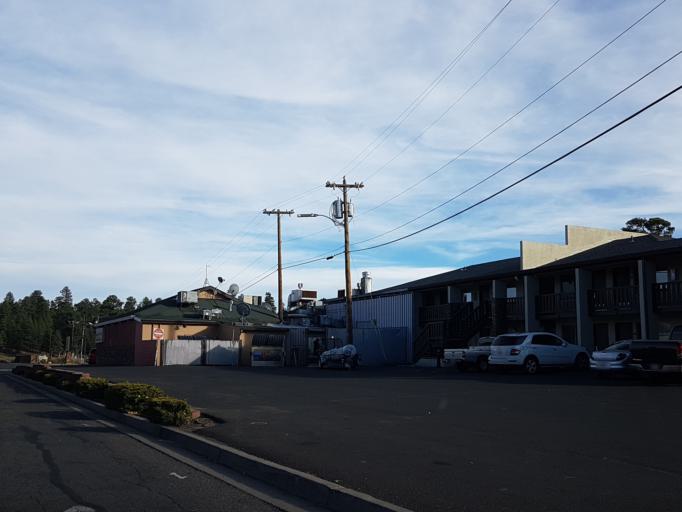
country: US
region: Arizona
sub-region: Coconino County
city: Grand Canyon Village
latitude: 35.9733
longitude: -112.1276
